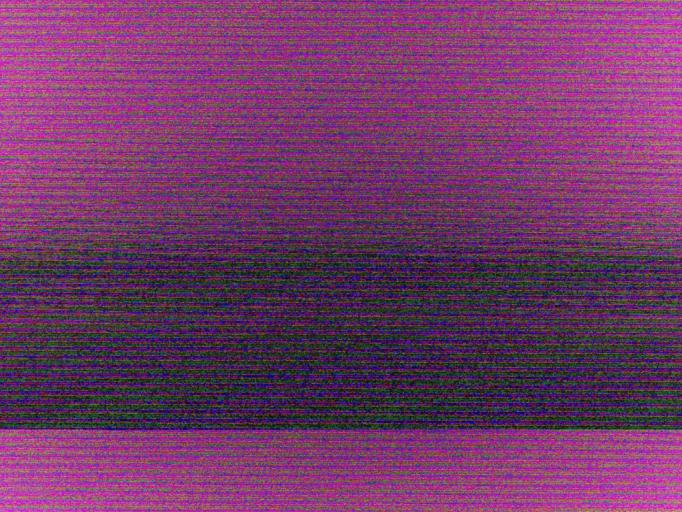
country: US
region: Massachusetts
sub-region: Middlesex County
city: Somerville
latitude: 42.3931
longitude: -71.1060
